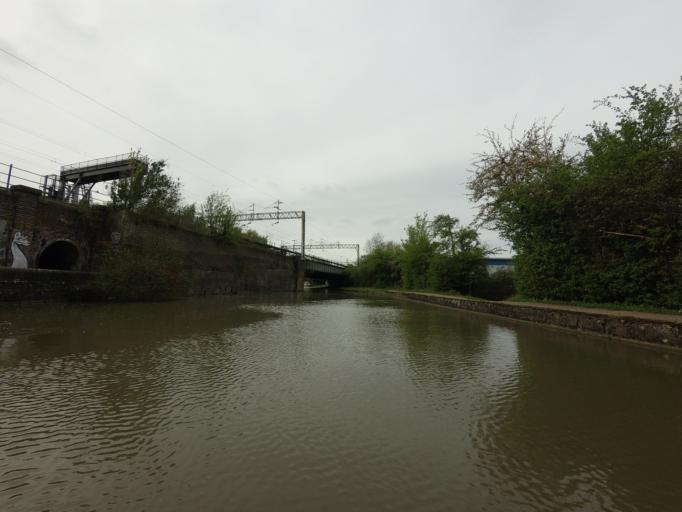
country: GB
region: England
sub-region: Milton Keynes
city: Bradwell
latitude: 52.0610
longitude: -0.8022
